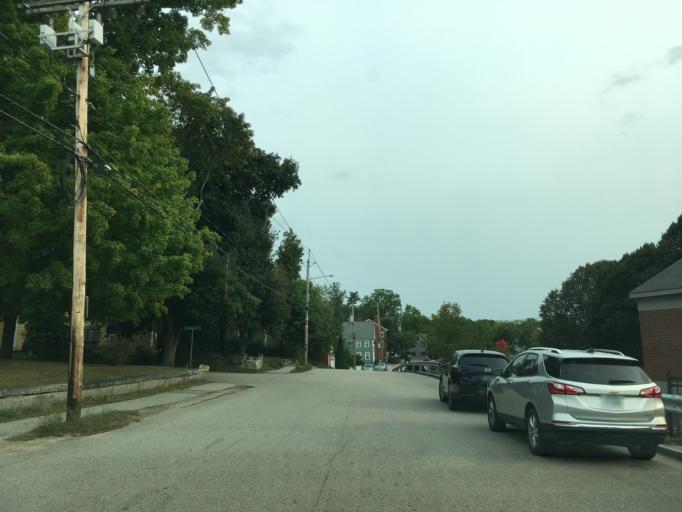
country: US
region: New Hampshire
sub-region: Rockingham County
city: Exeter
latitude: 42.9823
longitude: -70.9445
